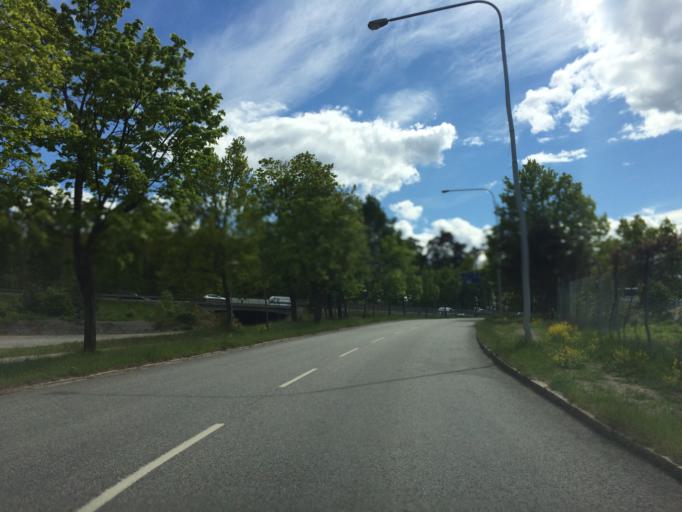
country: SE
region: Stockholm
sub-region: Botkyrka Kommun
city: Fittja
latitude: 59.2562
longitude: 17.8813
